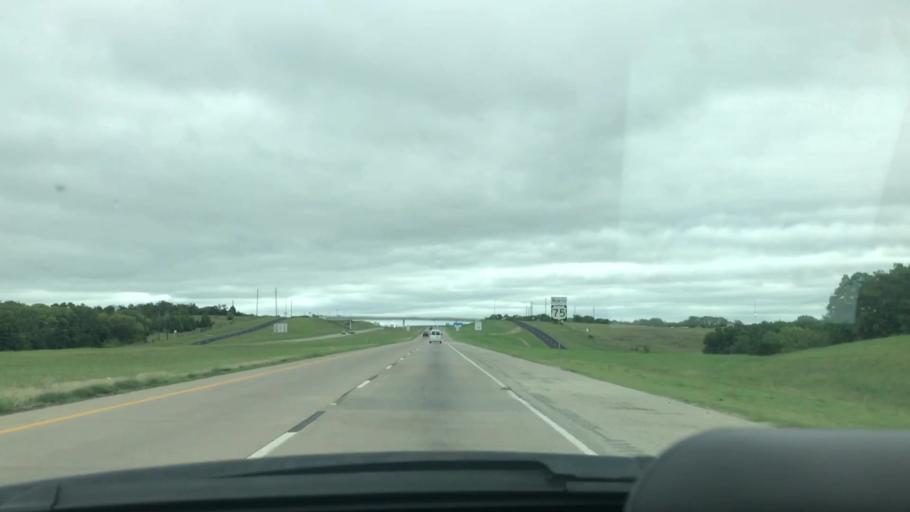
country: US
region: Texas
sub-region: Grayson County
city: Sherman
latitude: 33.6885
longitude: -96.6027
